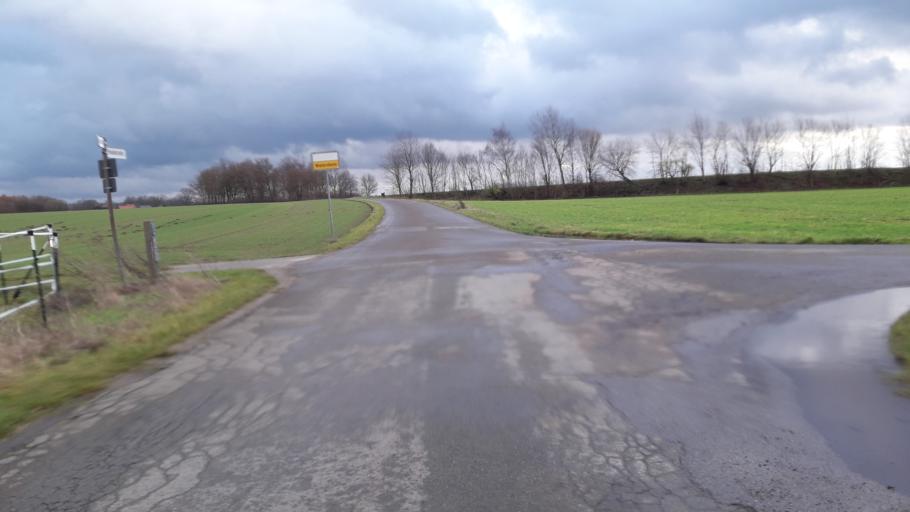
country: DE
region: North Rhine-Westphalia
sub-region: Regierungsbezirk Detmold
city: Petershagen
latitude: 52.3331
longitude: 8.9590
